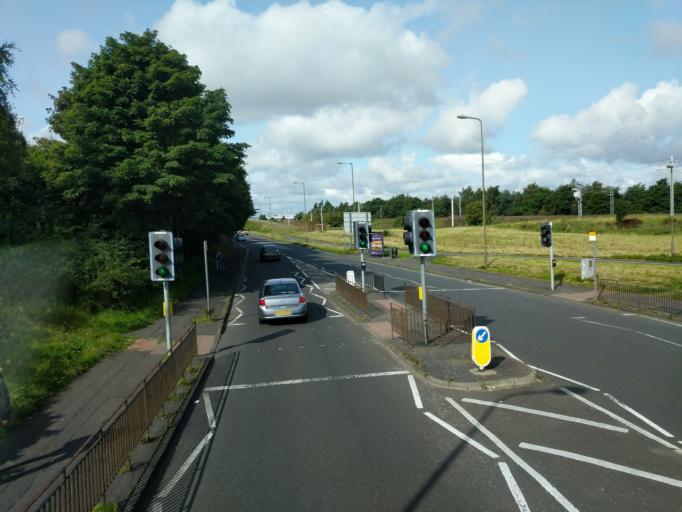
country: GB
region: Scotland
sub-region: Edinburgh
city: Colinton
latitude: 55.9294
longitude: -3.2859
